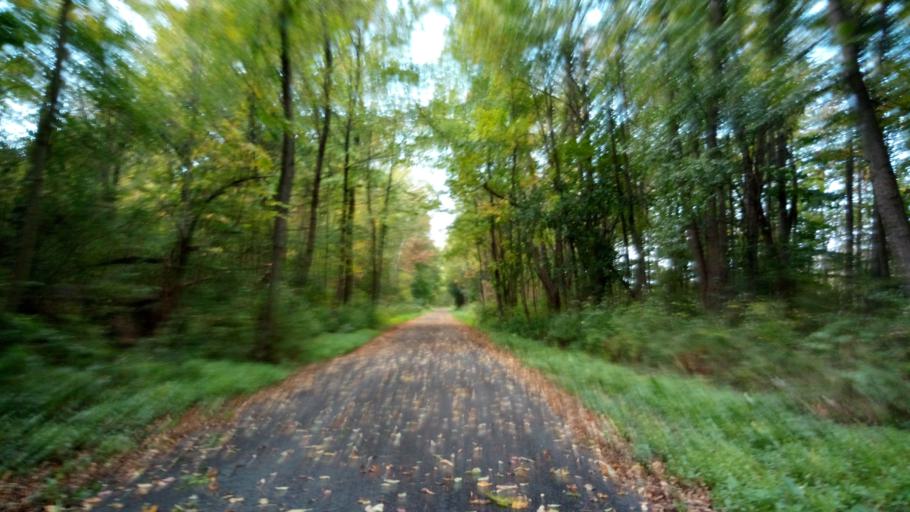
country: US
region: New York
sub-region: Wayne County
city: Clyde
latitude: 43.0662
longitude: -76.8493
